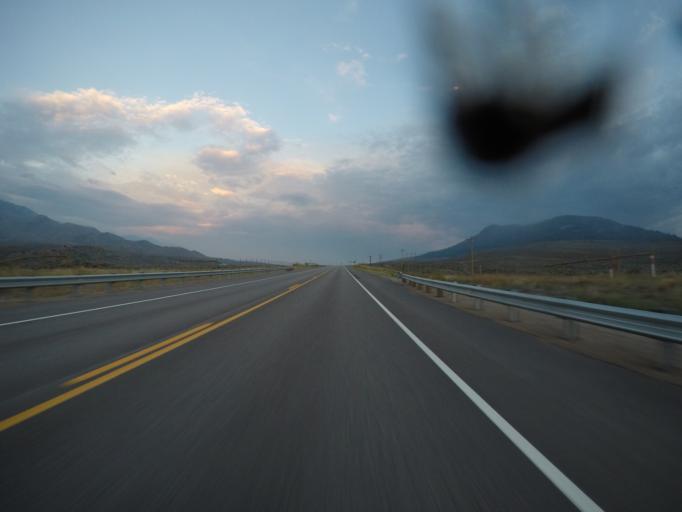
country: US
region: Colorado
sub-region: Grand County
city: Kremmling
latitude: 39.9167
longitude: -106.3285
